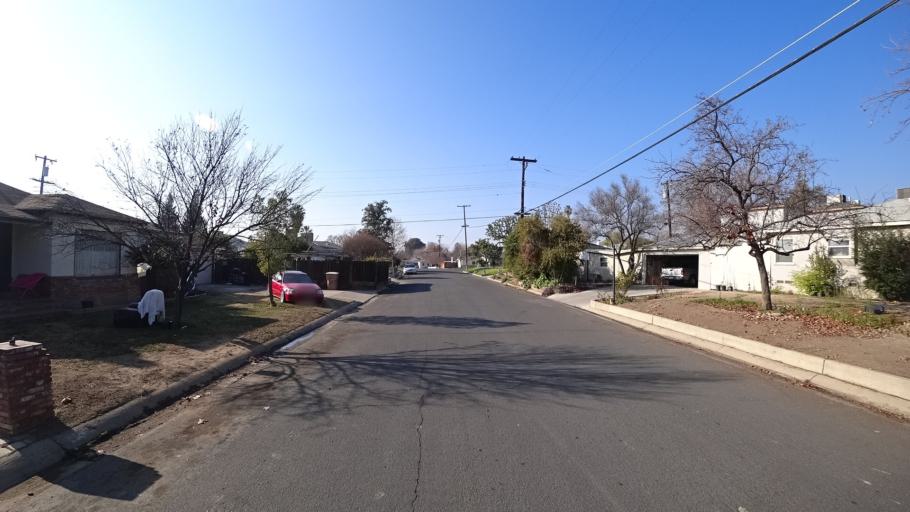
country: US
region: California
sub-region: Kern County
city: Bakersfield
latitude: 35.3952
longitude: -118.9964
